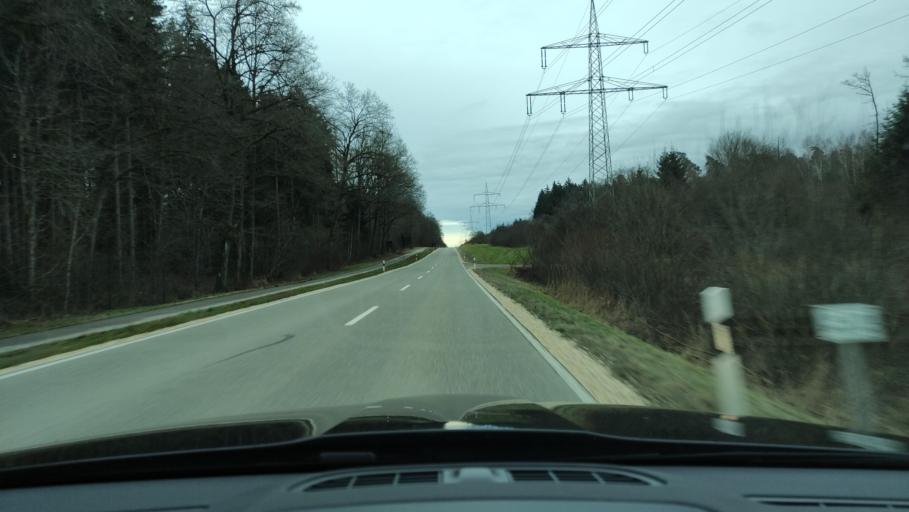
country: DE
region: Bavaria
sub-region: Swabia
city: Roggenburg
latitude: 48.2412
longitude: 10.2456
